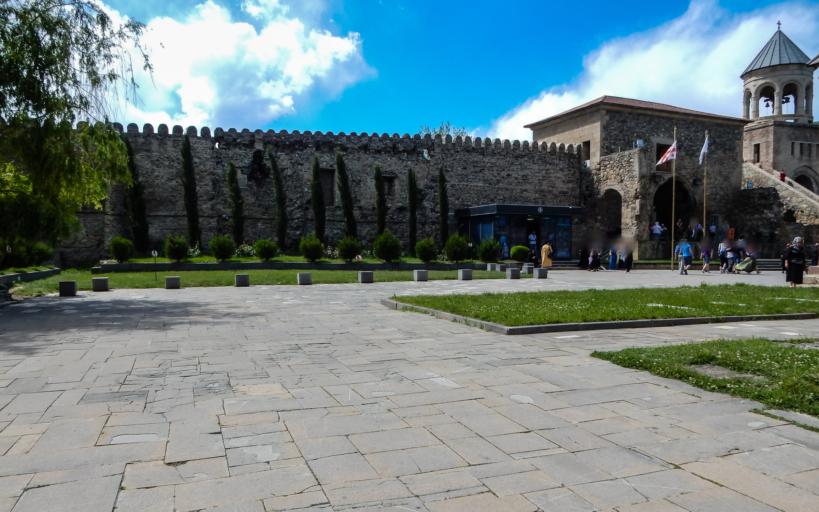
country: GE
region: Mtskheta-Mtianeti
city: Mtskheta
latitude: 41.8421
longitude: 44.7208
